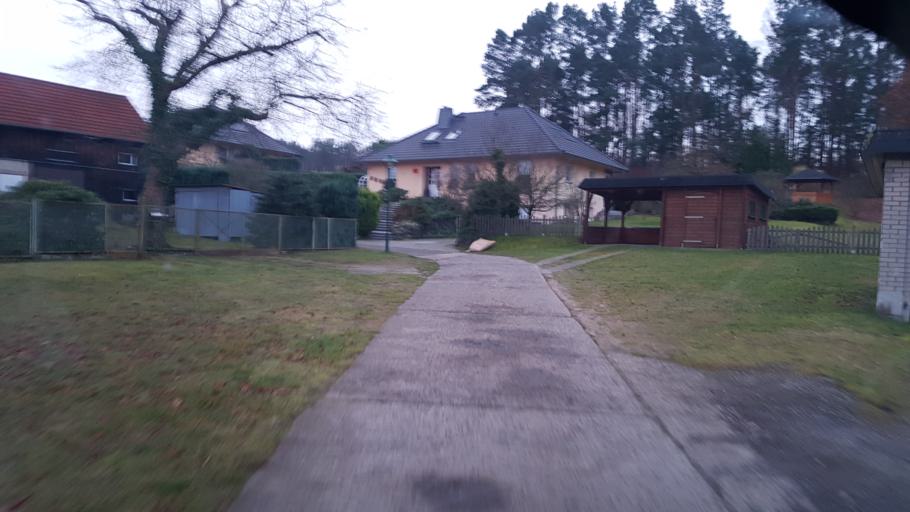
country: DE
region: Brandenburg
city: Mixdorf
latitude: 52.1093
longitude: 14.4918
